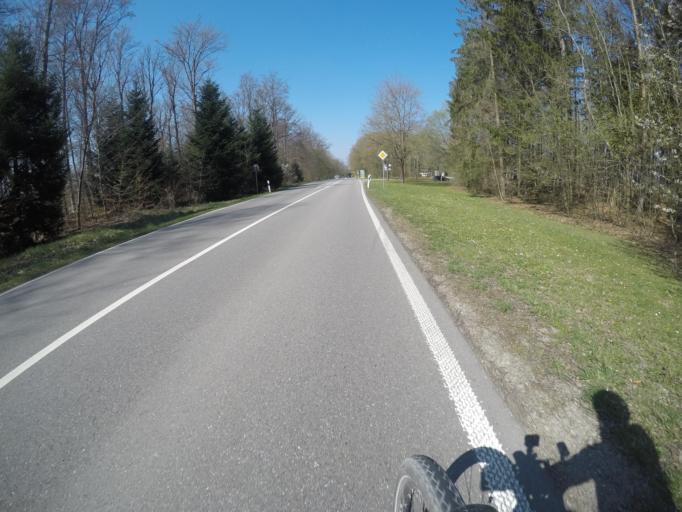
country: DE
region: Baden-Wuerttemberg
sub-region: Regierungsbezirk Stuttgart
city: Leonberg
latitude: 48.7628
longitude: 9.0008
